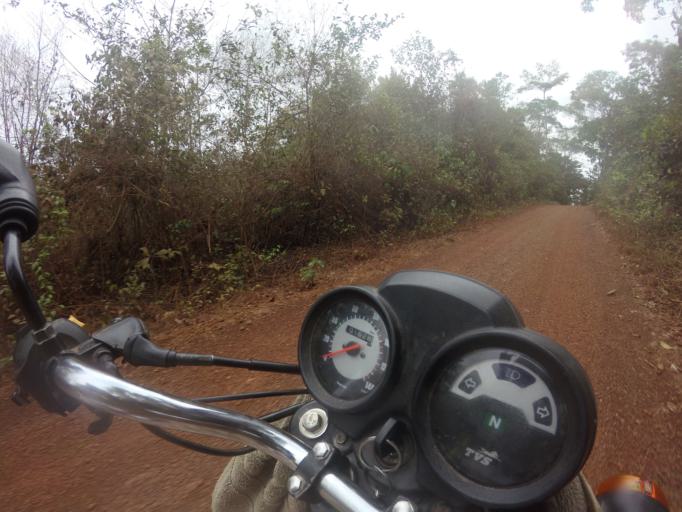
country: SL
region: Southern Province
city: Zimmi
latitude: 7.2165
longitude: -11.1847
